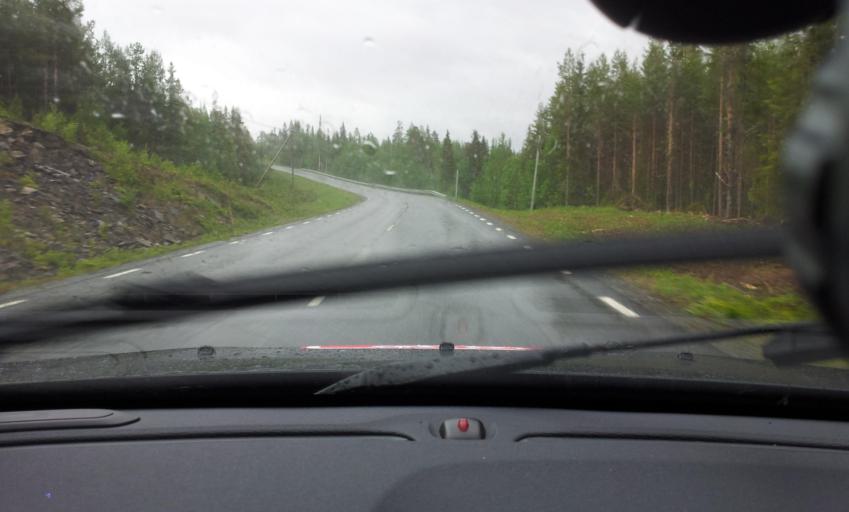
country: SE
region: Jaemtland
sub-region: Are Kommun
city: Are
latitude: 63.2329
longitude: 13.1653
